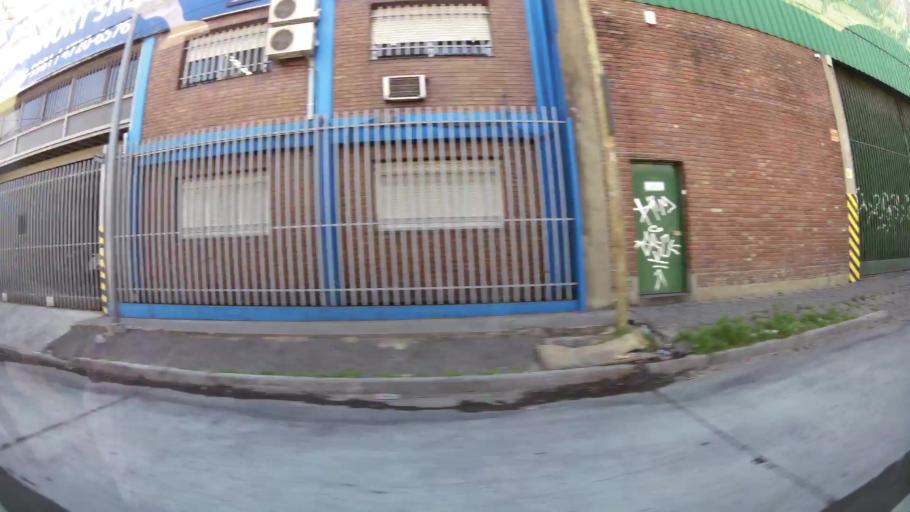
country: AR
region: Buenos Aires
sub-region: Partido de General San Martin
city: General San Martin
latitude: -34.5189
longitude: -58.5694
